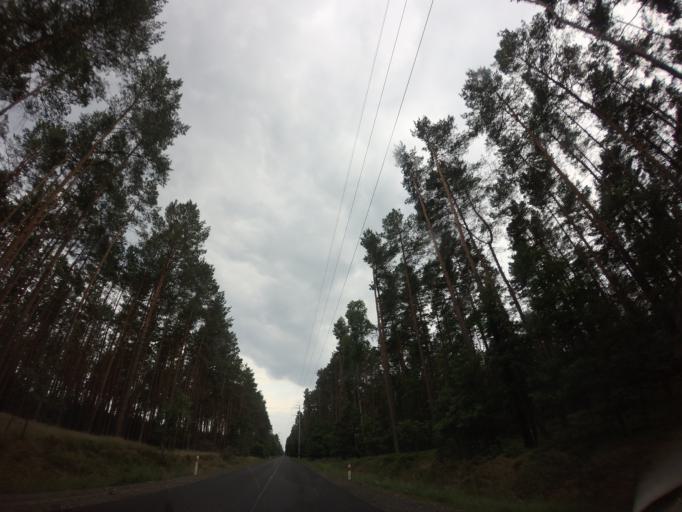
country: PL
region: West Pomeranian Voivodeship
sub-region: Powiat drawski
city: Czaplinek
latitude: 53.4763
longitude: 16.2254
